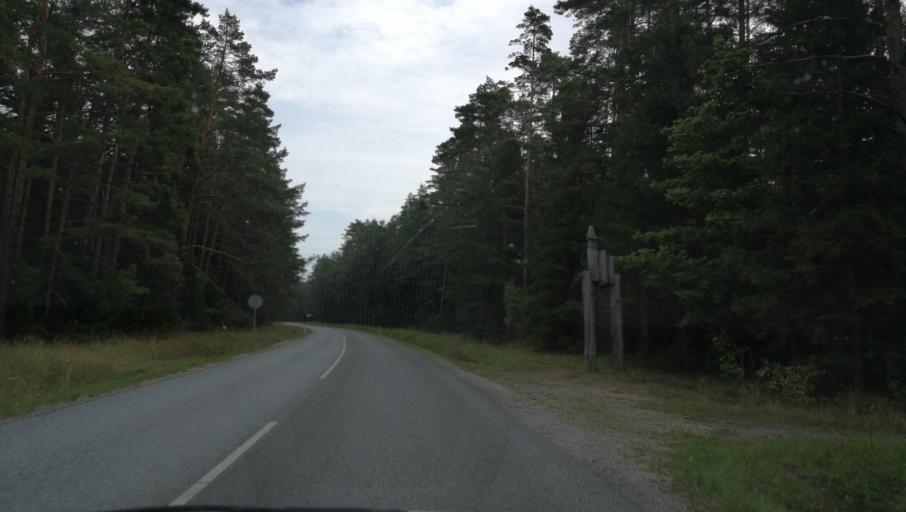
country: LV
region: Alsunga
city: Alsunga
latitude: 57.0110
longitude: 21.4032
